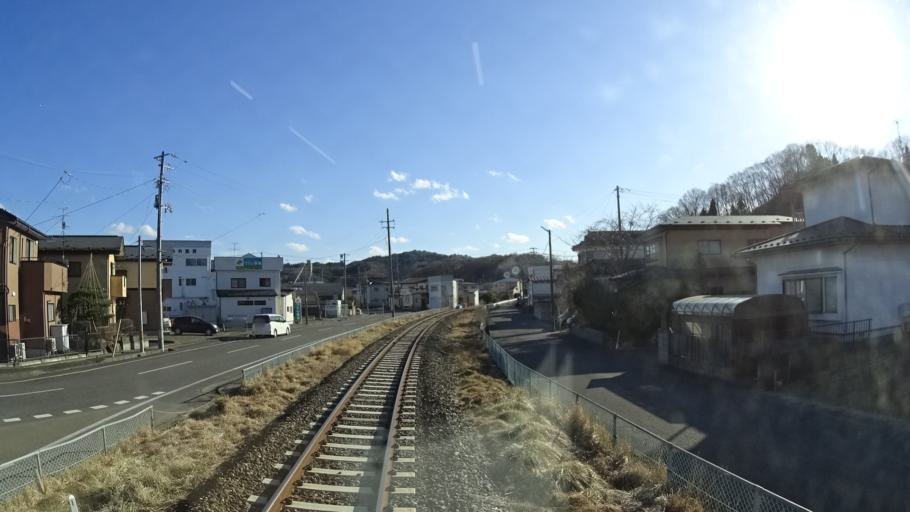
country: JP
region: Iwate
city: Miyako
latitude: 39.6280
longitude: 141.9603
